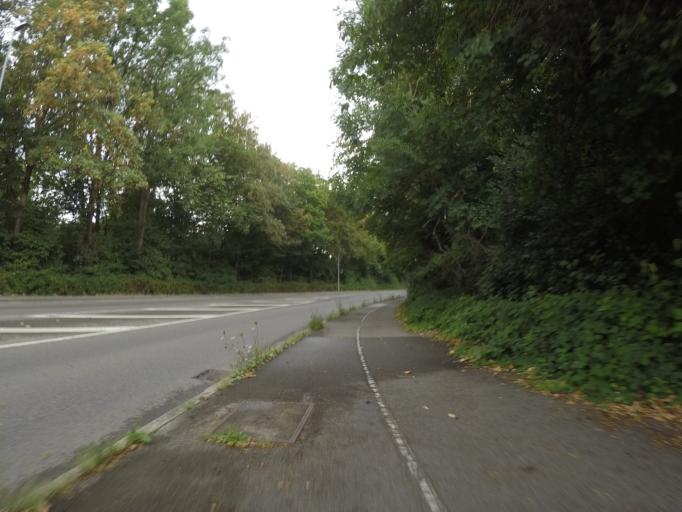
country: DE
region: Baden-Wuerttemberg
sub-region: Tuebingen Region
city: Reutlingen
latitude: 48.4832
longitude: 9.1966
